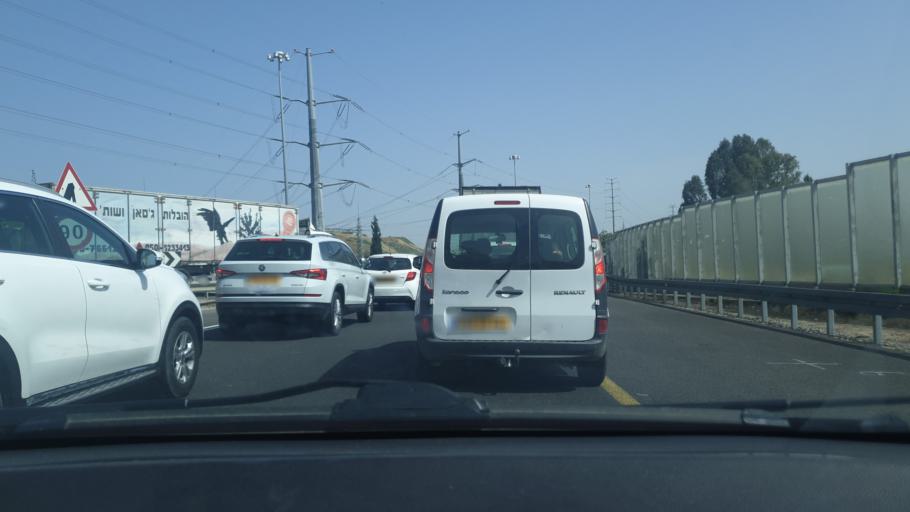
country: IL
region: Tel Aviv
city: Azor
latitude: 32.0193
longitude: 34.8225
